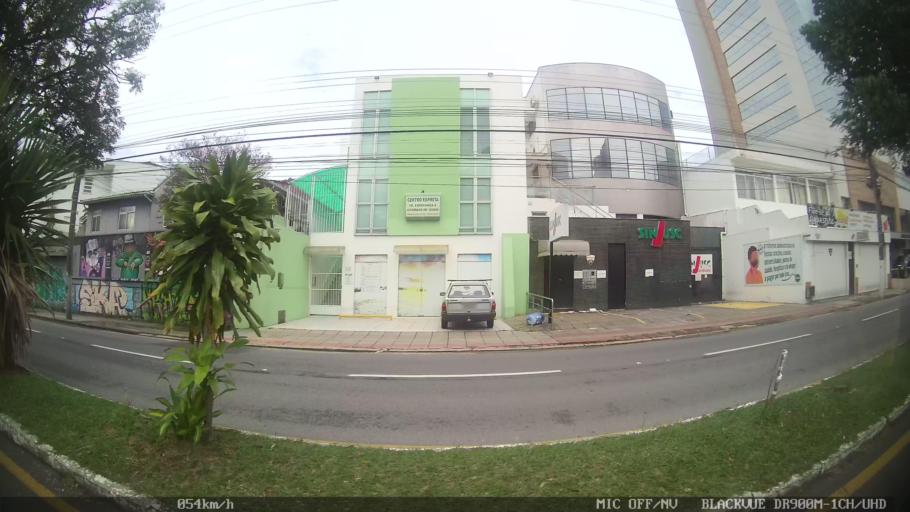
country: BR
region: Santa Catarina
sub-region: Florianopolis
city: Florianopolis
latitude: -27.5976
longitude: -48.5445
